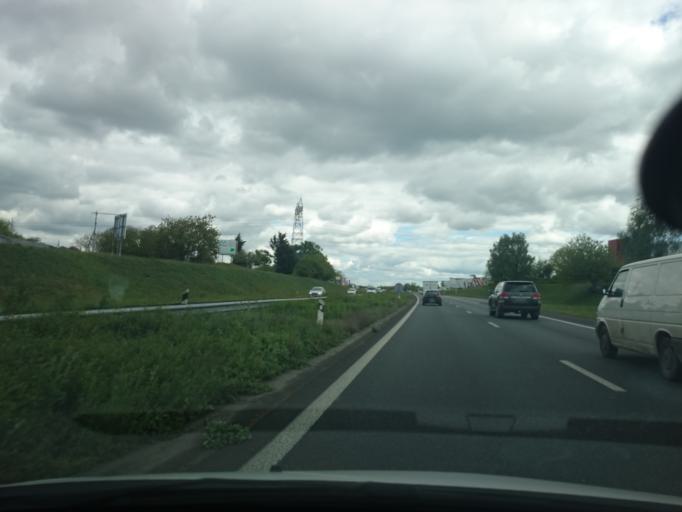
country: FR
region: Pays de la Loire
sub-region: Departement de la Loire-Atlantique
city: Sautron
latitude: 47.2413
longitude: -1.6677
